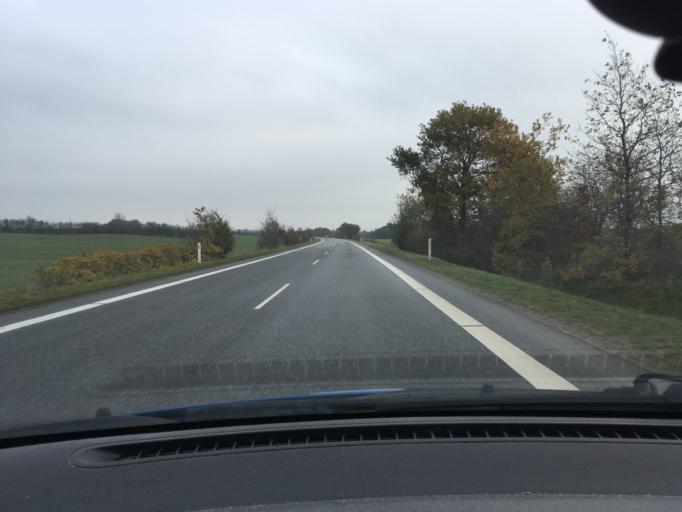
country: DK
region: South Denmark
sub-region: Aabenraa Kommune
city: Aabenraa
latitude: 54.9857
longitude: 9.3945
